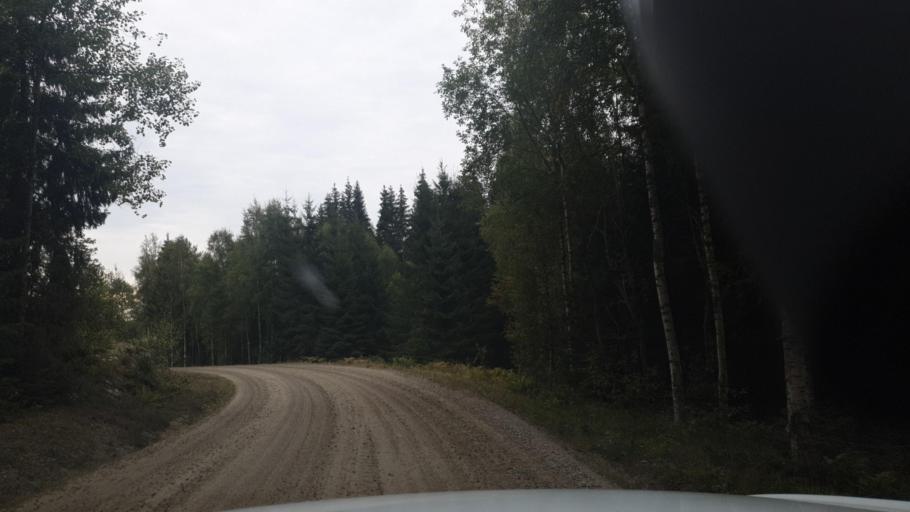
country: SE
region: Vaermland
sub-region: Karlstads Kommun
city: Edsvalla
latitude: 59.4954
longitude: 13.0288
